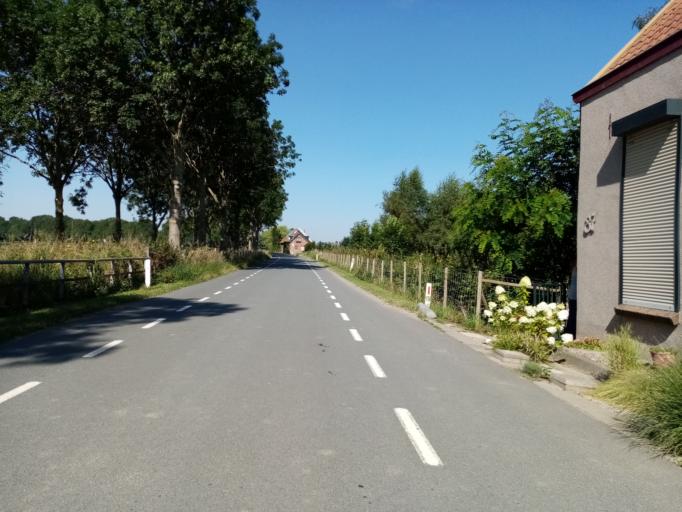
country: NL
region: North Brabant
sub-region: Gemeente Moerdijk
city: Klundert
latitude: 51.6568
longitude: 4.6254
